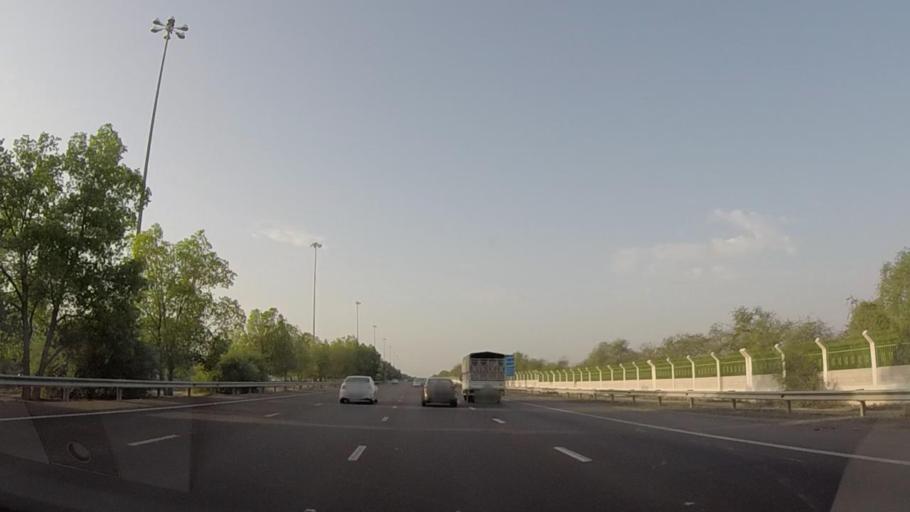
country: AE
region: Dubai
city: Dubai
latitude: 24.7787
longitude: 54.8531
